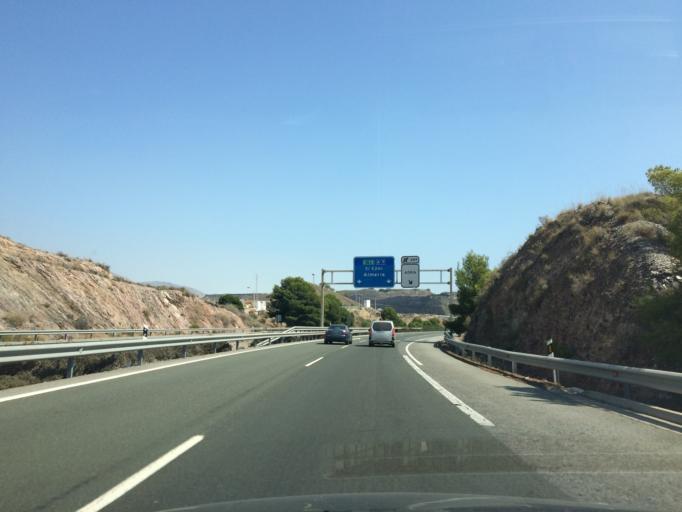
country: ES
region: Andalusia
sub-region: Provincia de Almeria
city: Adra
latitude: 36.7613
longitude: -3.0073
